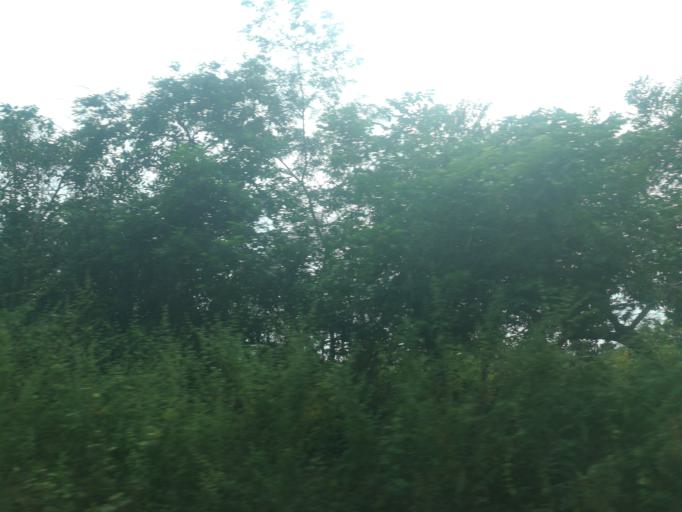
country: NG
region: Ogun
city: Ayetoro
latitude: 7.2909
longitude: 3.0805
